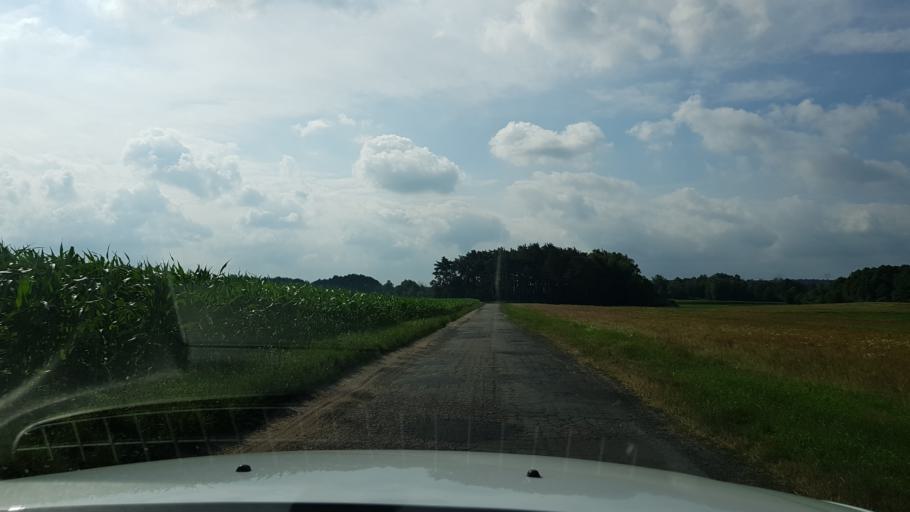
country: PL
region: West Pomeranian Voivodeship
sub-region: Powiat gryfinski
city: Gryfino
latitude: 53.2163
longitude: 14.5502
